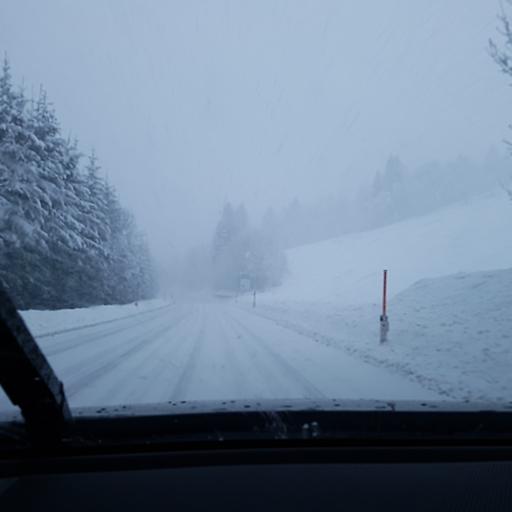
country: AT
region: Salzburg
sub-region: Politischer Bezirk Salzburg-Umgebung
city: Strobl
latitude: 47.5929
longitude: 13.4833
